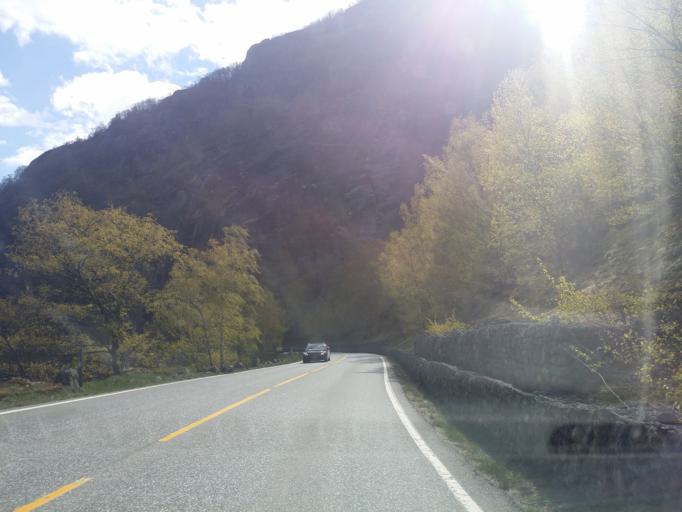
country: NO
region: Hordaland
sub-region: Eidfjord
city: Eidfjord
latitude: 60.4547
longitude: 7.0923
